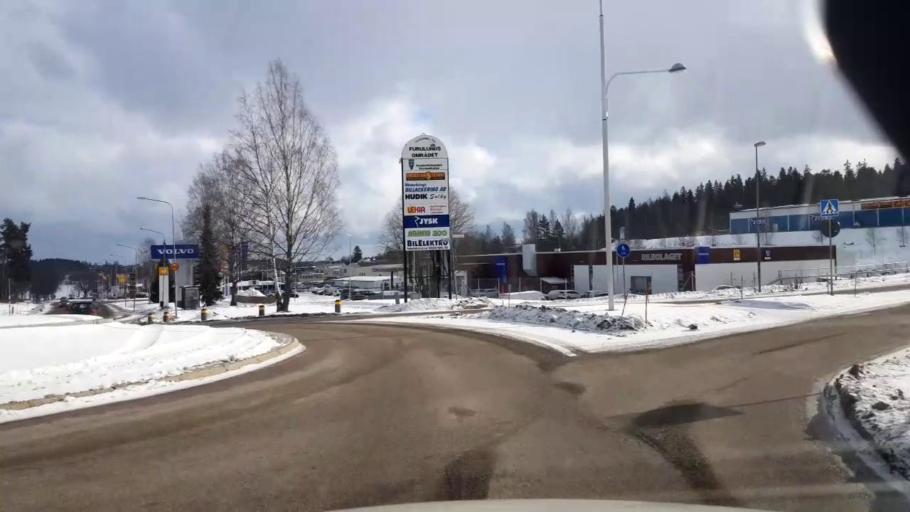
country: SE
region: Gaevleborg
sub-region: Hudiksvalls Kommun
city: Hudiksvall
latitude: 61.7354
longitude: 17.0948
